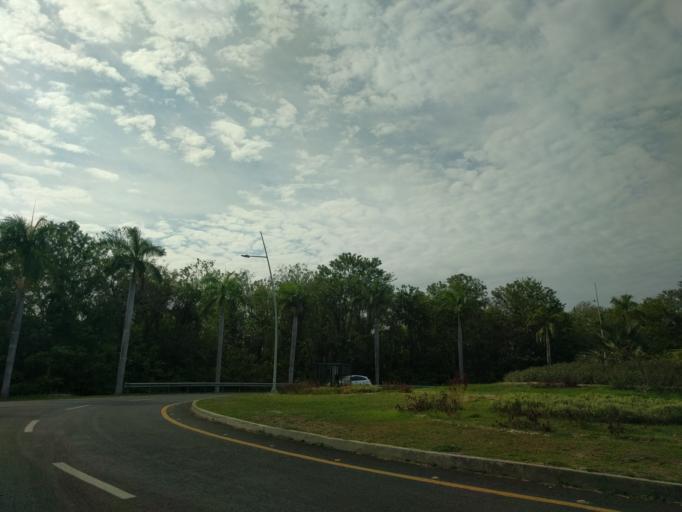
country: PA
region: Panama
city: Tocumen
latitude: 9.0590
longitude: -79.3982
